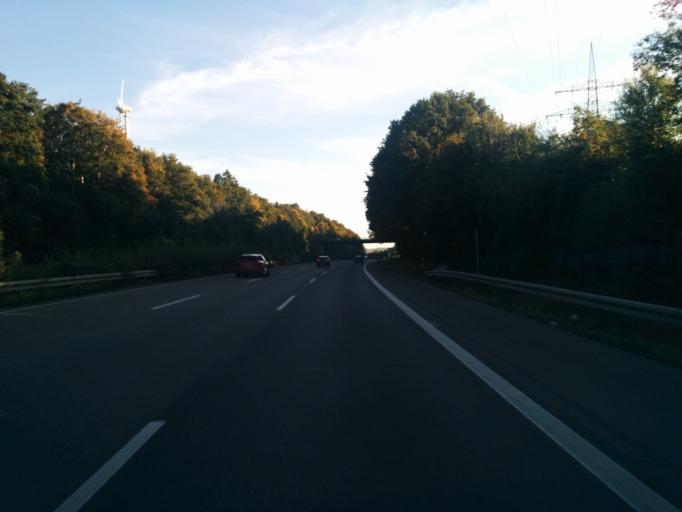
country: DE
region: North Rhine-Westphalia
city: Witten
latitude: 51.4853
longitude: 7.3908
